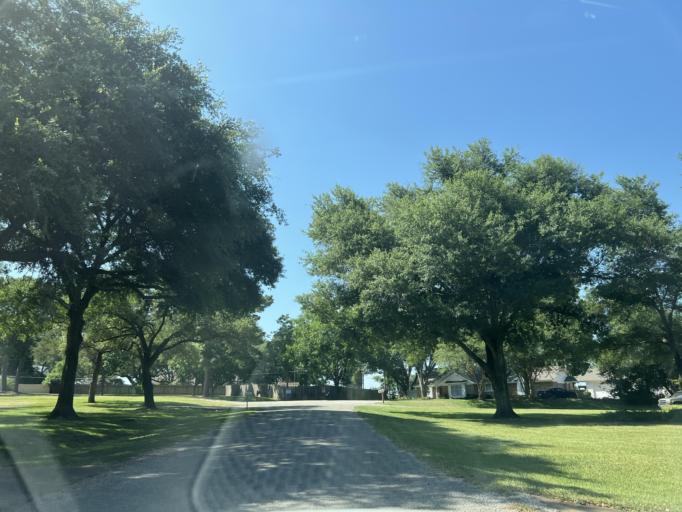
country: US
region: Texas
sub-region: Washington County
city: Brenham
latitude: 30.1523
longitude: -96.3612
